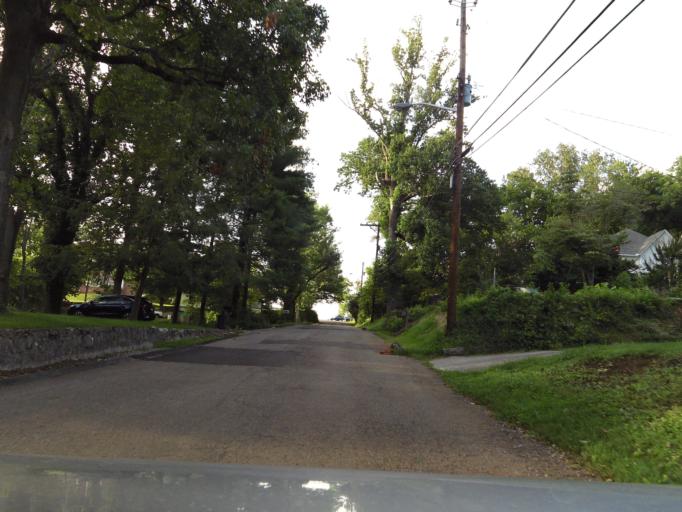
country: US
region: Tennessee
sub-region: Knox County
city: Knoxville
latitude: 35.9546
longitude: -83.8790
